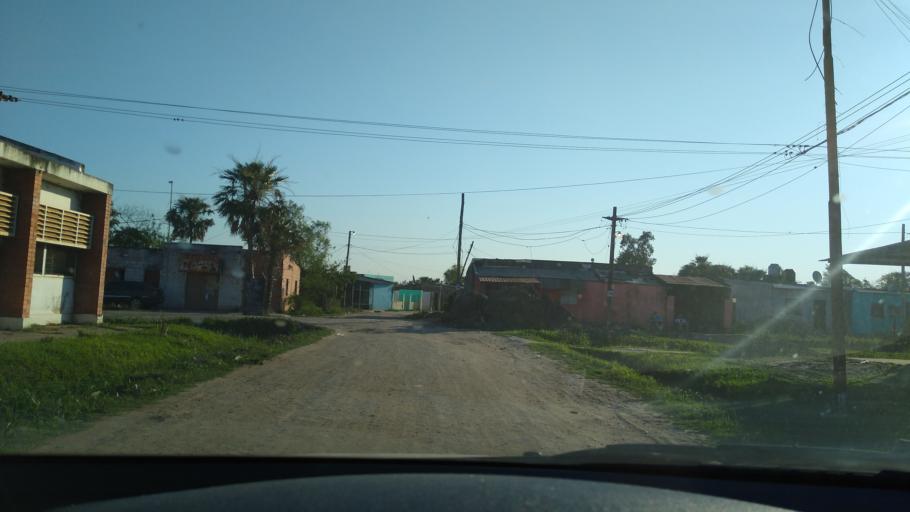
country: AR
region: Chaco
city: Puerto Vilelas
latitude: -27.5132
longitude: -58.9448
